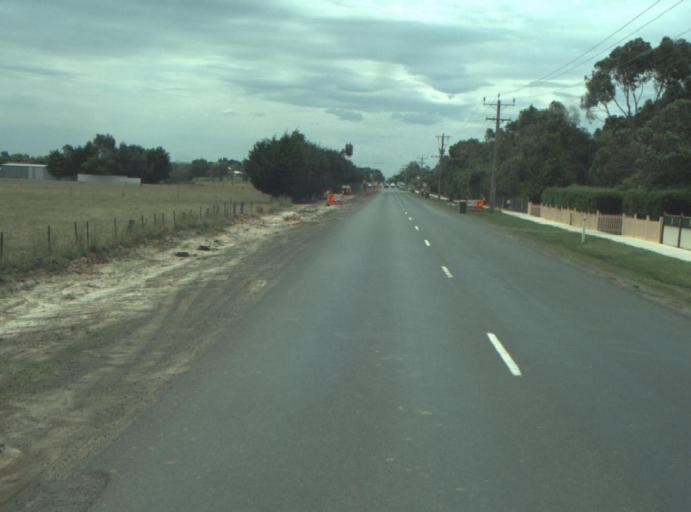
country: AU
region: Victoria
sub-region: Greater Geelong
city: Leopold
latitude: -38.1923
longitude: 144.4544
